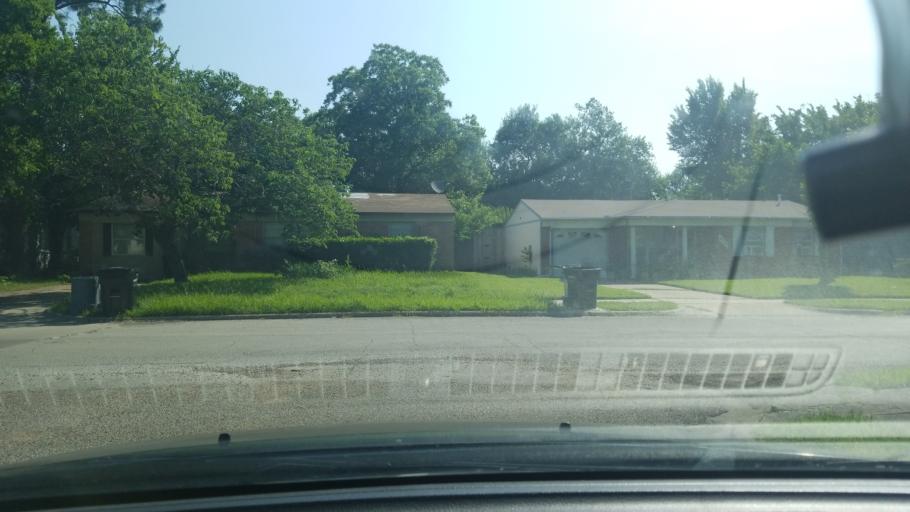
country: US
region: Texas
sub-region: Dallas County
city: Mesquite
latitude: 32.8302
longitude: -96.6415
